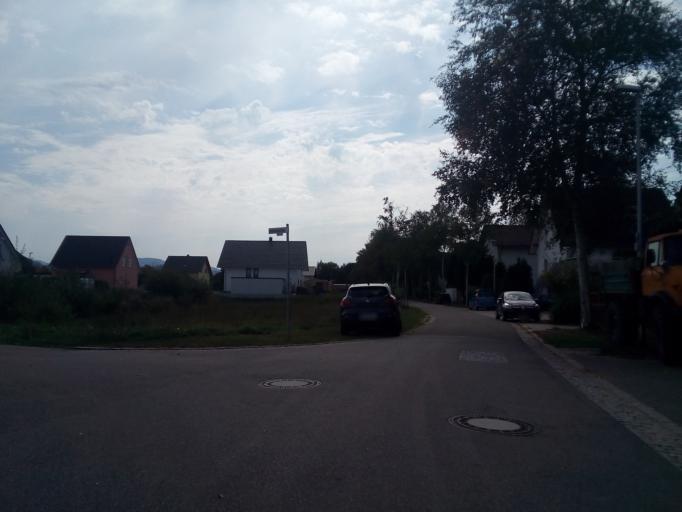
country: DE
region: Baden-Wuerttemberg
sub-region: Freiburg Region
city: Sasbach
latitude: 48.6562
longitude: 8.0857
